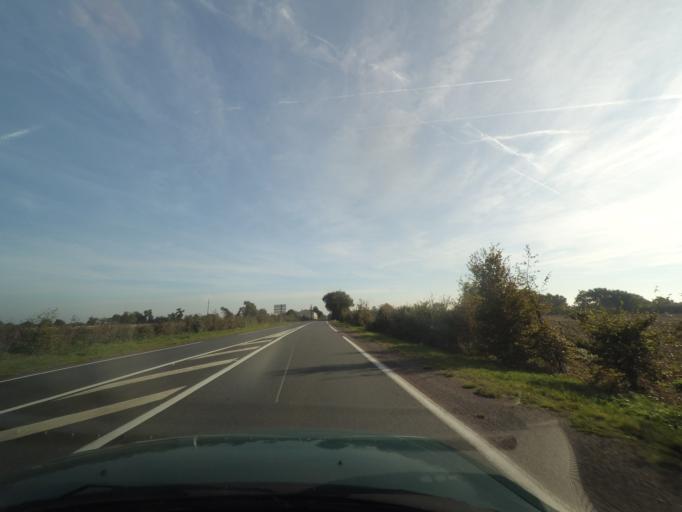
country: FR
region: Pays de la Loire
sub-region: Departement de la Vendee
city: La Bruffiere
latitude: 46.9866
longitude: -1.1987
